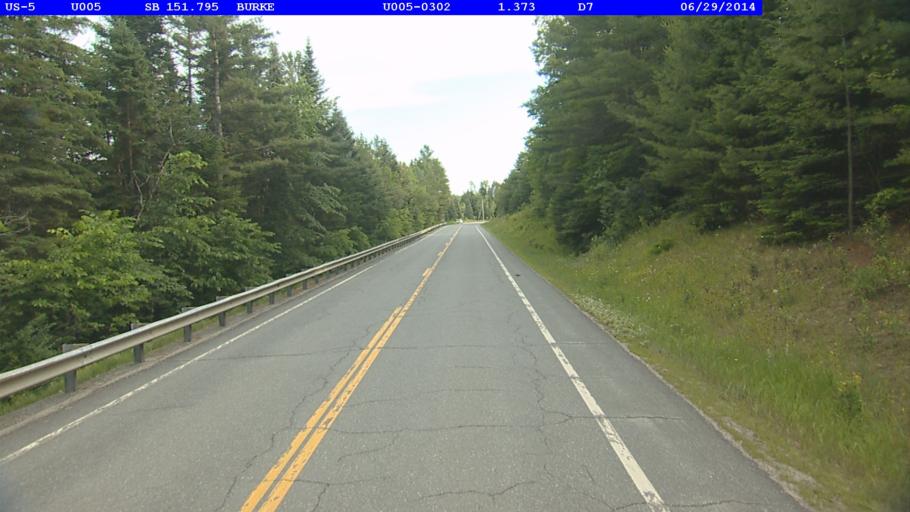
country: US
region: Vermont
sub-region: Caledonia County
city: Lyndonville
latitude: 44.6048
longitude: -71.9712
